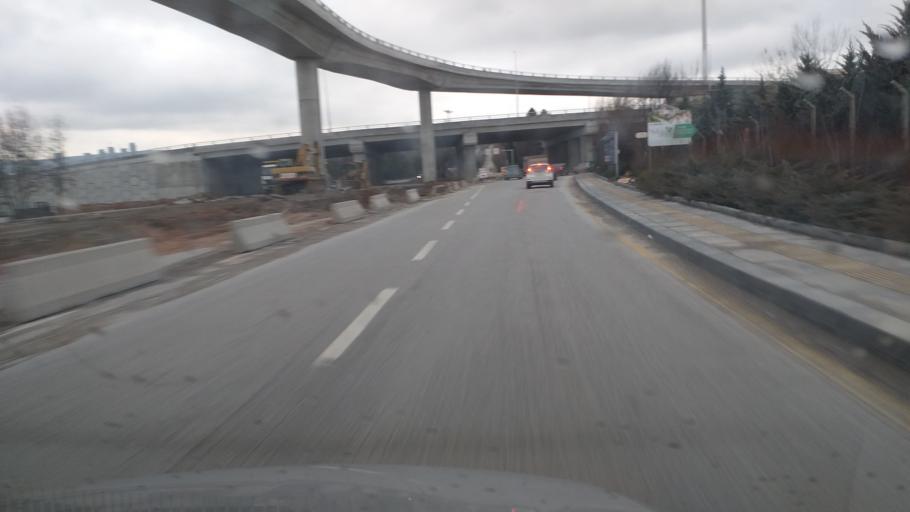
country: TR
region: Ankara
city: Batikent
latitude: 39.8977
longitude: 32.7334
